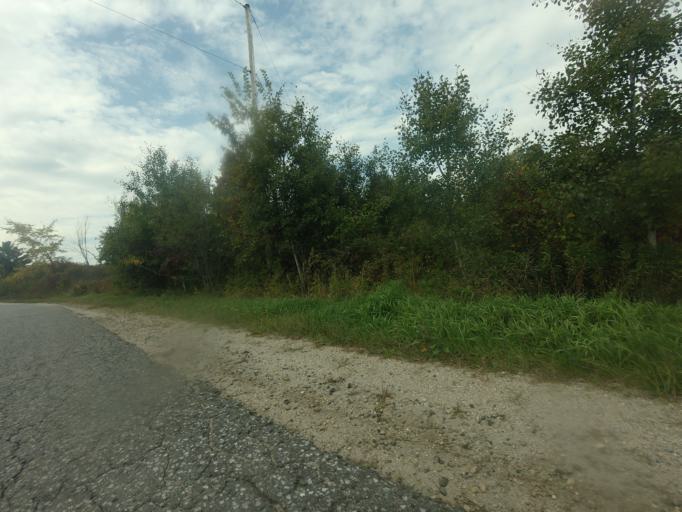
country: CA
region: Quebec
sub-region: Outaouais
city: Wakefield
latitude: 45.9735
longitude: -75.9362
